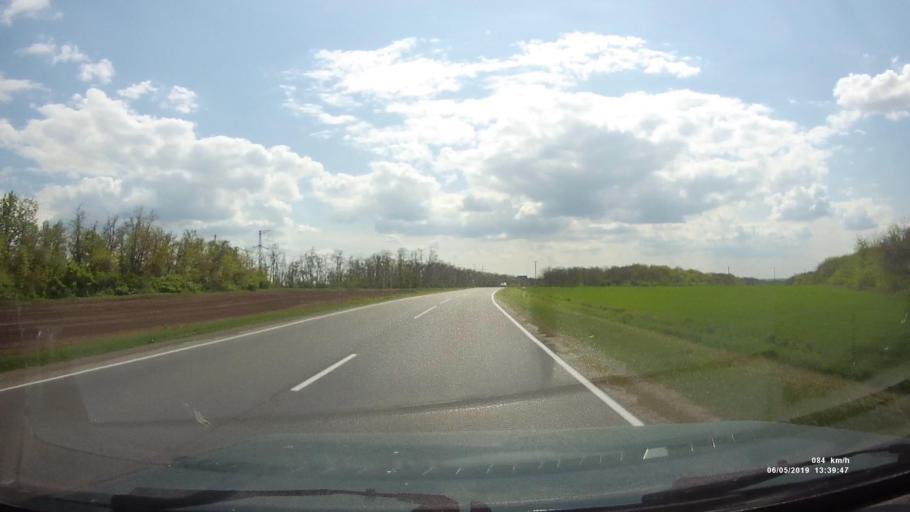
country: RU
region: Rostov
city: Ust'-Donetskiy
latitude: 47.6719
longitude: 40.7009
